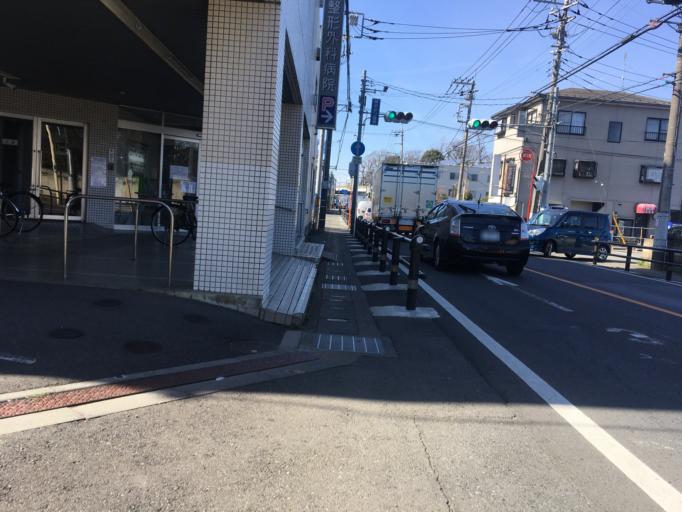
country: JP
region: Saitama
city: Shiki
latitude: 35.8033
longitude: 139.5641
